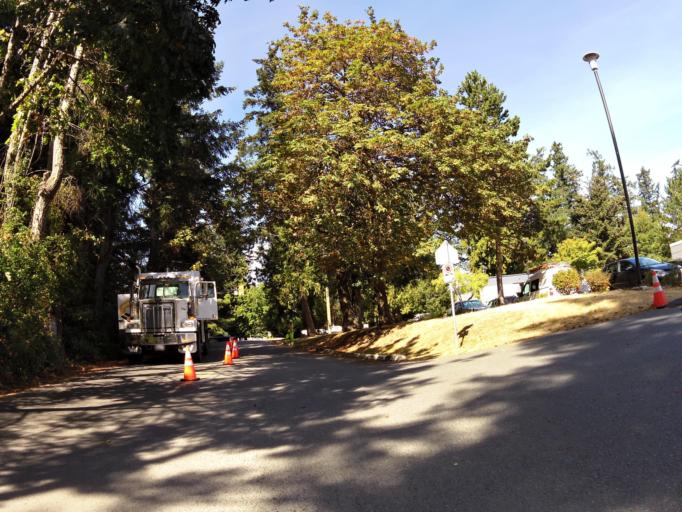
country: CA
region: British Columbia
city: Victoria
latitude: 48.5008
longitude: -123.3613
